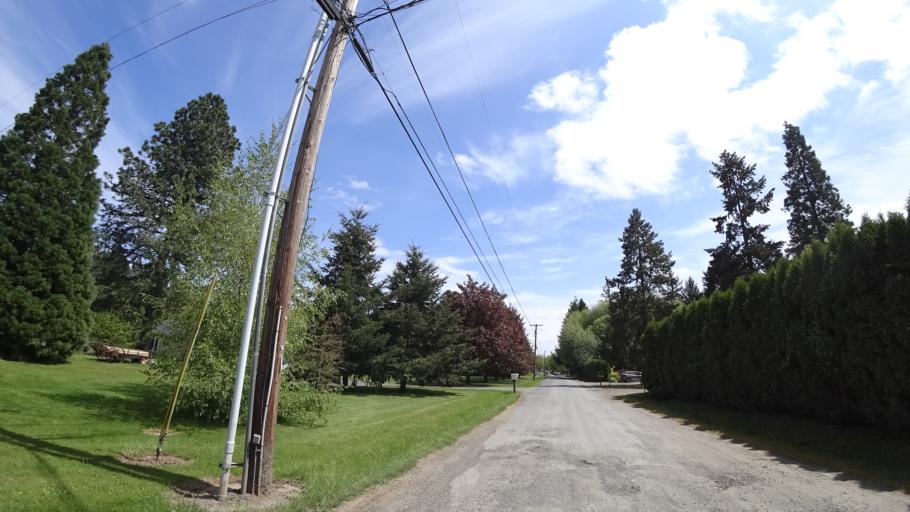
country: US
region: Oregon
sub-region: Washington County
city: Aloha
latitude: 45.4751
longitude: -122.8969
